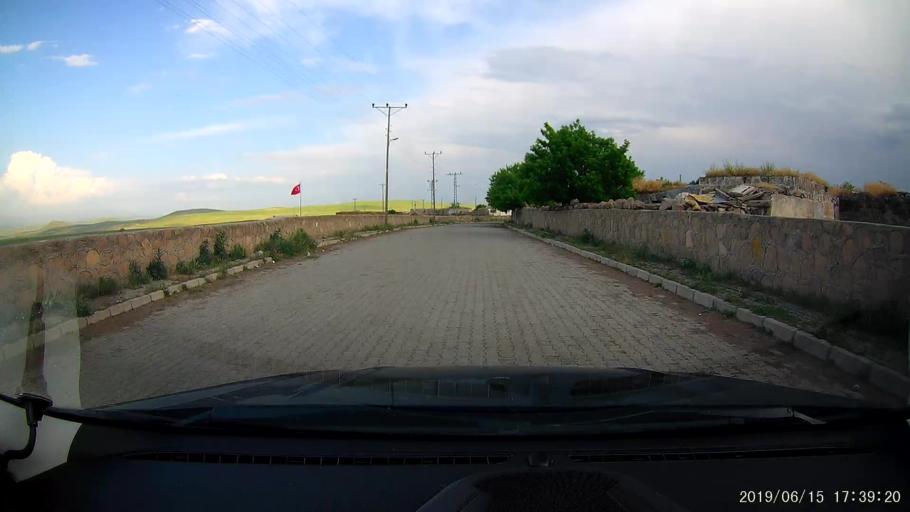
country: TR
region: Kars
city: Basgedikler
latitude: 40.5165
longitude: 43.5699
